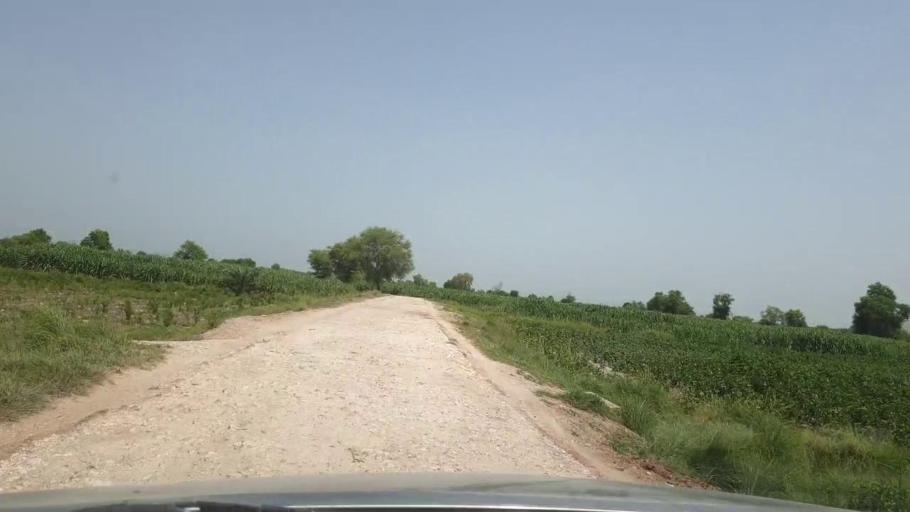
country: PK
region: Sindh
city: Pano Aqil
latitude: 27.8212
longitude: 69.2236
